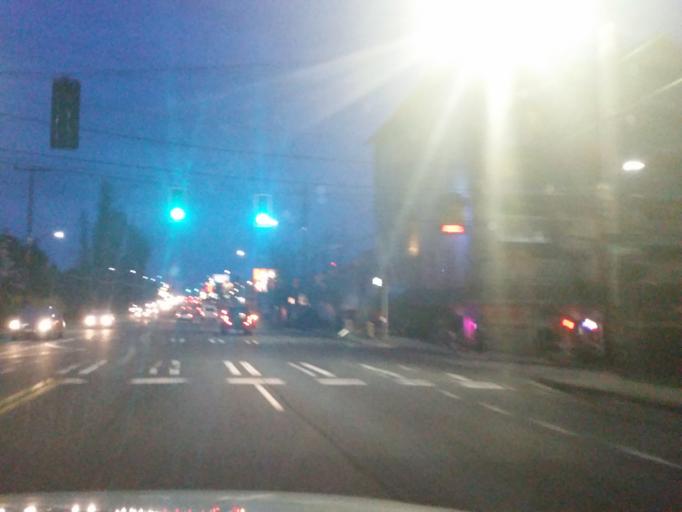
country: US
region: Washington
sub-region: King County
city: Shoreline
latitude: 47.7122
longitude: -122.3448
